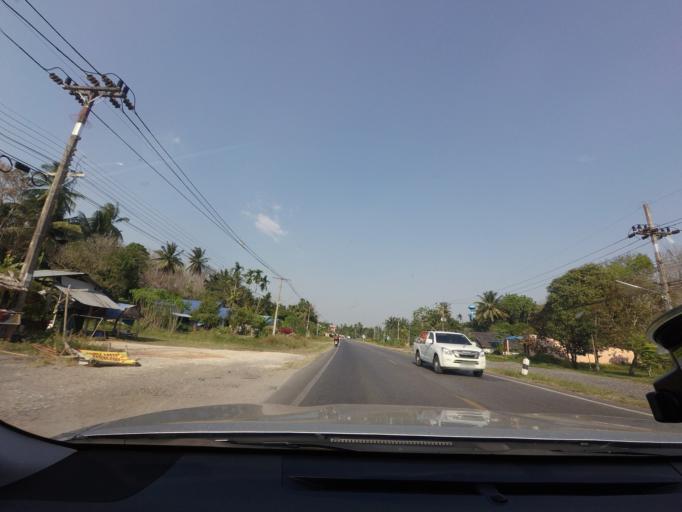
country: TH
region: Surat Thani
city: Phrasaeng
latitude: 8.5674
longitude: 99.1900
